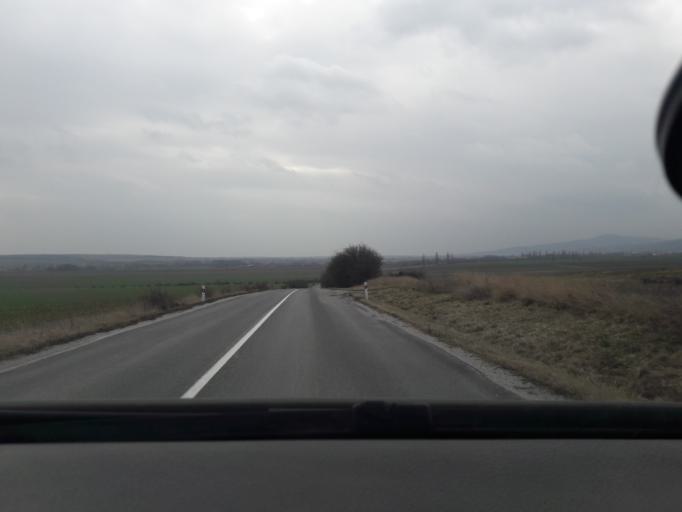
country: SK
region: Trnavsky
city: Smolenice
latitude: 48.4329
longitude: 17.4225
